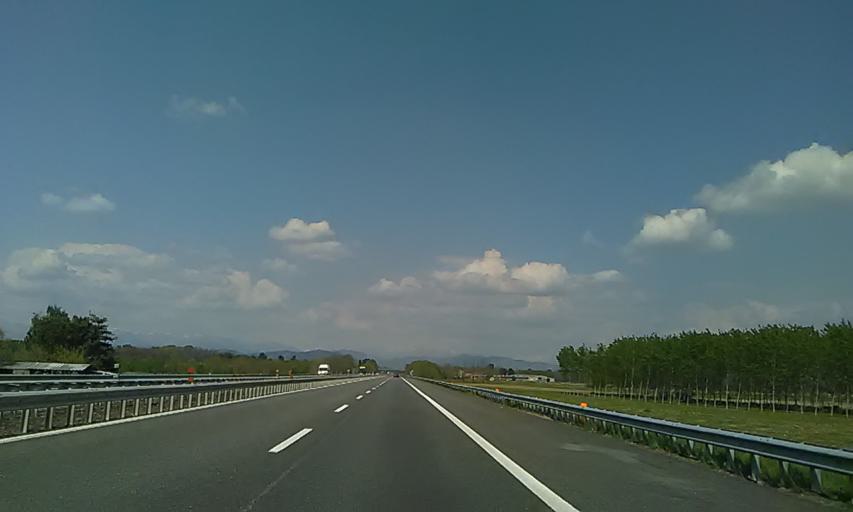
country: IT
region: Piedmont
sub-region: Provincia di Novara
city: Sizzano
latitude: 45.5613
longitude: 8.4168
